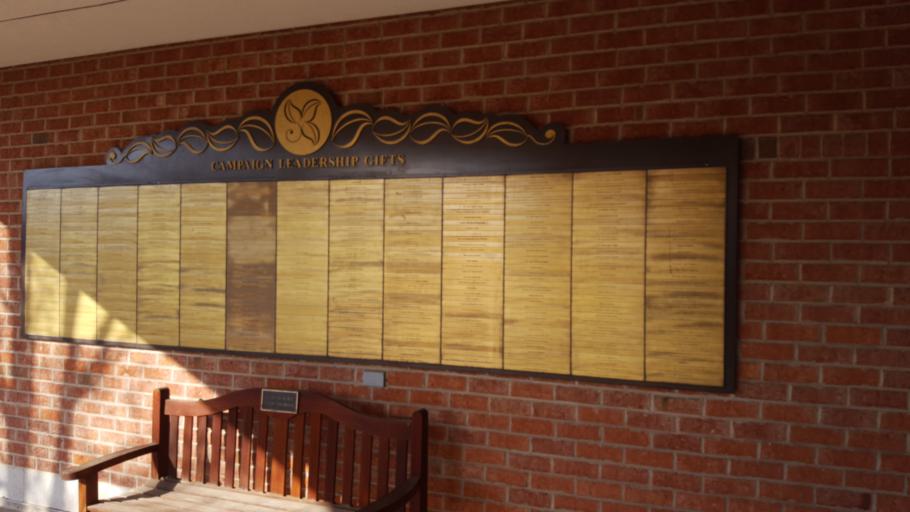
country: US
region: Illinois
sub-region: Cook County
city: Northfield
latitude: 42.0976
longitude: -87.8107
